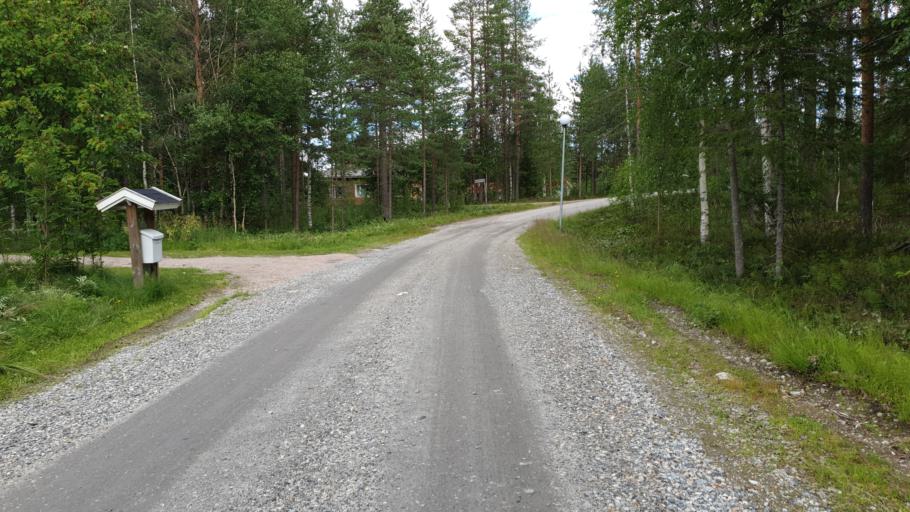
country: FI
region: Kainuu
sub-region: Kehys-Kainuu
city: Kuhmo
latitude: 64.3922
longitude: 29.8287
